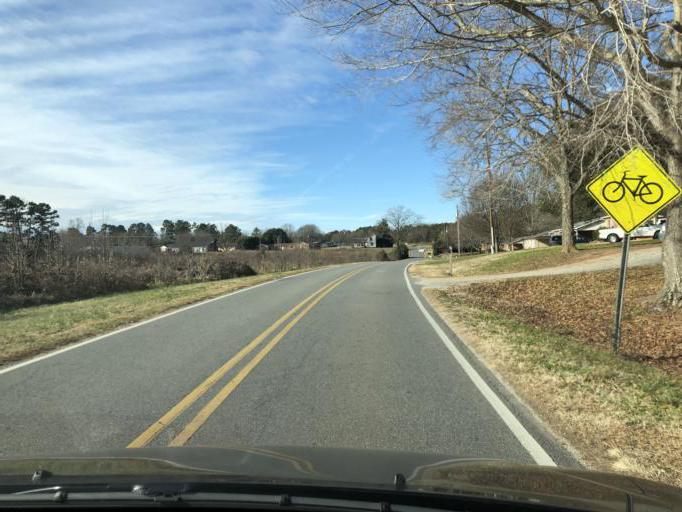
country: US
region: North Carolina
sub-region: Cleveland County
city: Boiling Springs
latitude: 35.2358
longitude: -81.6619
